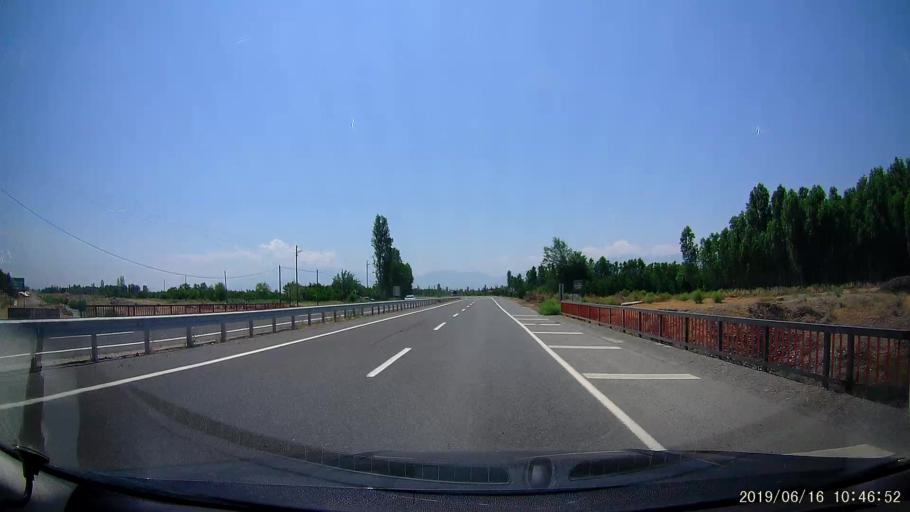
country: AM
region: Armavir
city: Shenavan
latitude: 40.0172
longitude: 43.8823
